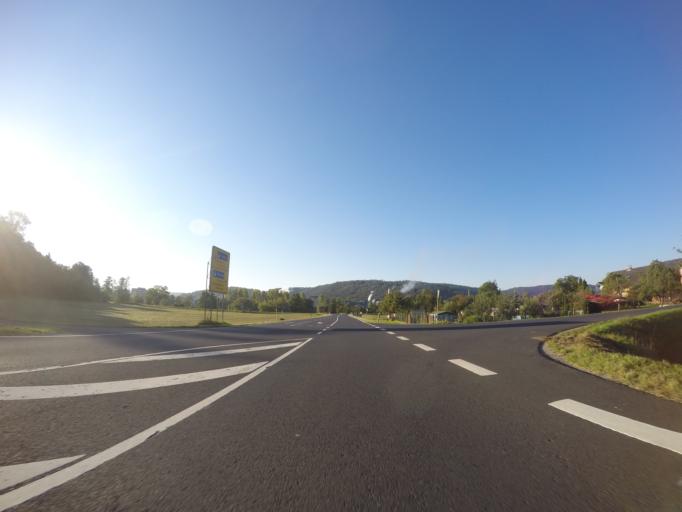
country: DE
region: Bavaria
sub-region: Regierungsbezirk Unterfranken
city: Hasloch
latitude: 49.7918
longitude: 9.4943
